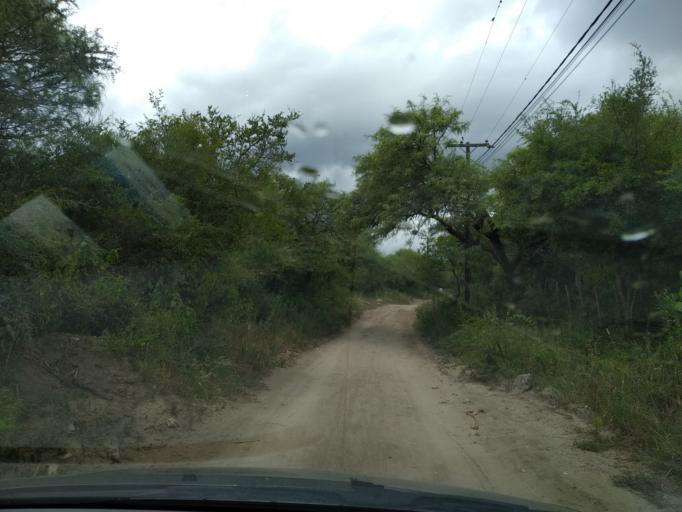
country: AR
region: Cordoba
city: Villa Las Rosas
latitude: -31.9430
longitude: -65.0328
